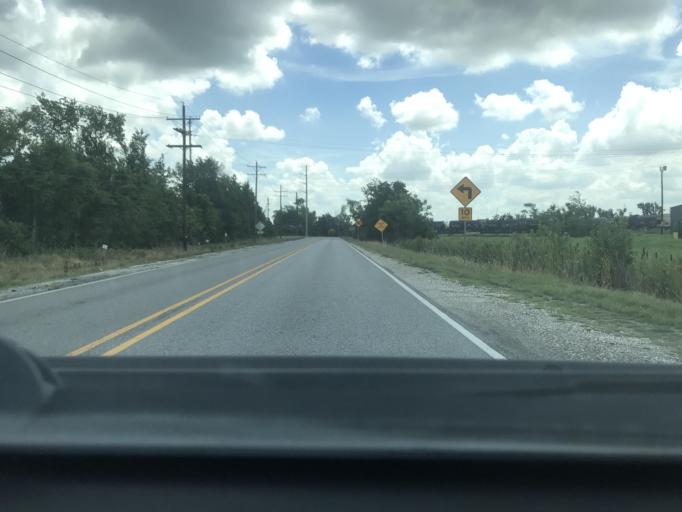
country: US
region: Louisiana
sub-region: Calcasieu Parish
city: Westlake
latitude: 30.2376
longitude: -93.2854
